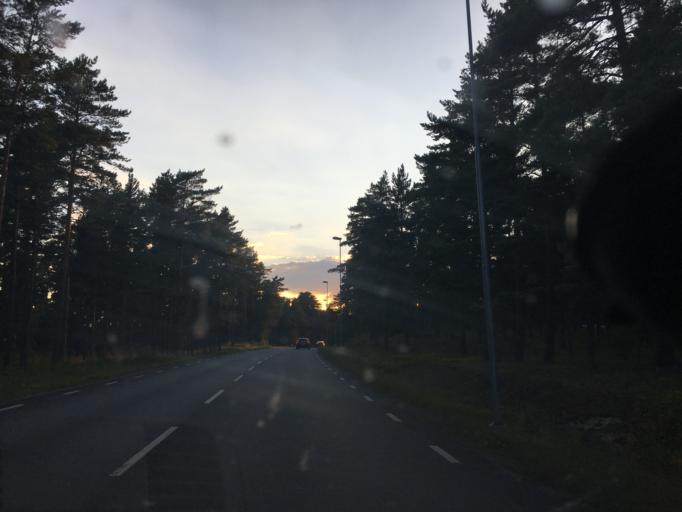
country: SE
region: Skane
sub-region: Kristianstads Kommun
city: Ahus
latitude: 55.9413
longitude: 14.3106
